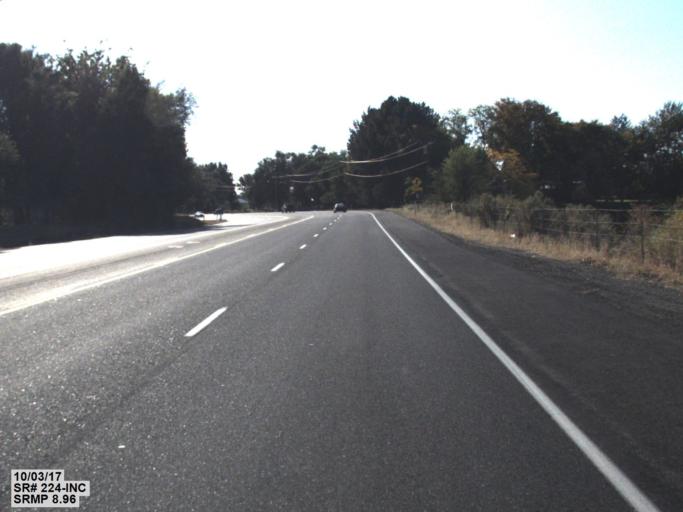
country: US
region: Washington
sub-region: Benton County
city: West Richland
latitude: 46.2954
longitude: -119.3236
